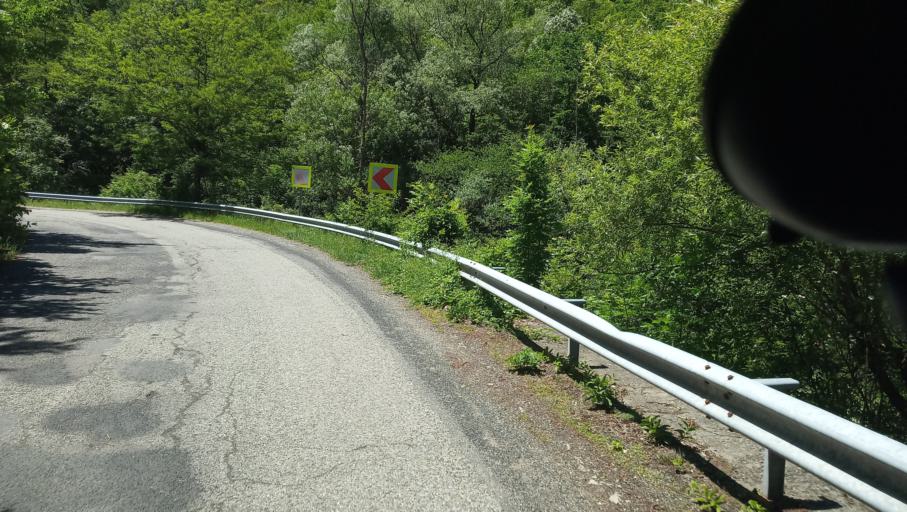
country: RO
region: Mehedinti
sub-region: Comuna Isverna
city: Isverna
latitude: 44.9962
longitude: 22.5244
